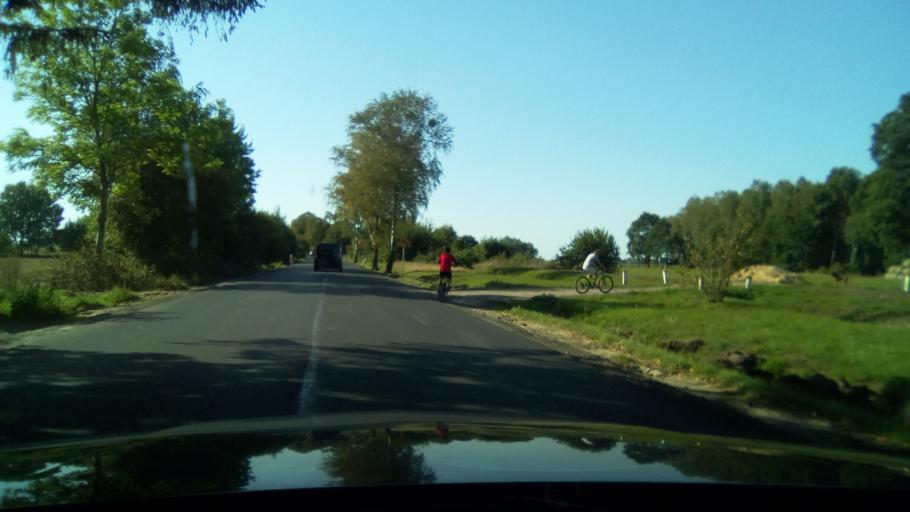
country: PL
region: West Pomeranian Voivodeship
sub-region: Powiat gryficki
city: Ploty
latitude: 53.8120
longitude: 15.1953
